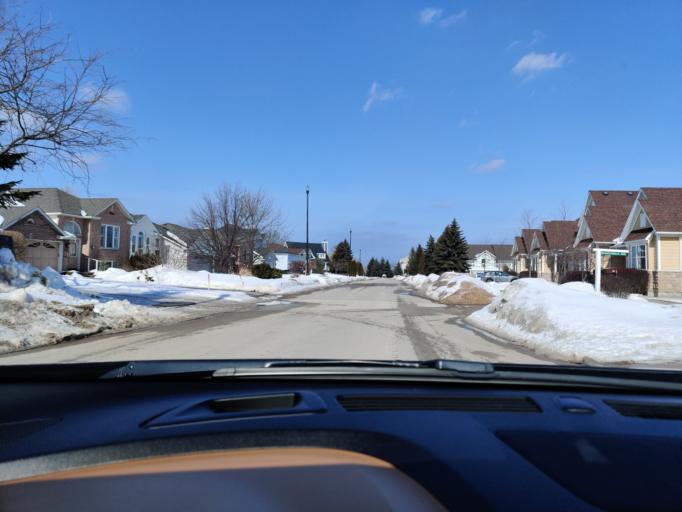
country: CA
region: Ontario
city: Collingwood
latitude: 44.5102
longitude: -80.2365
